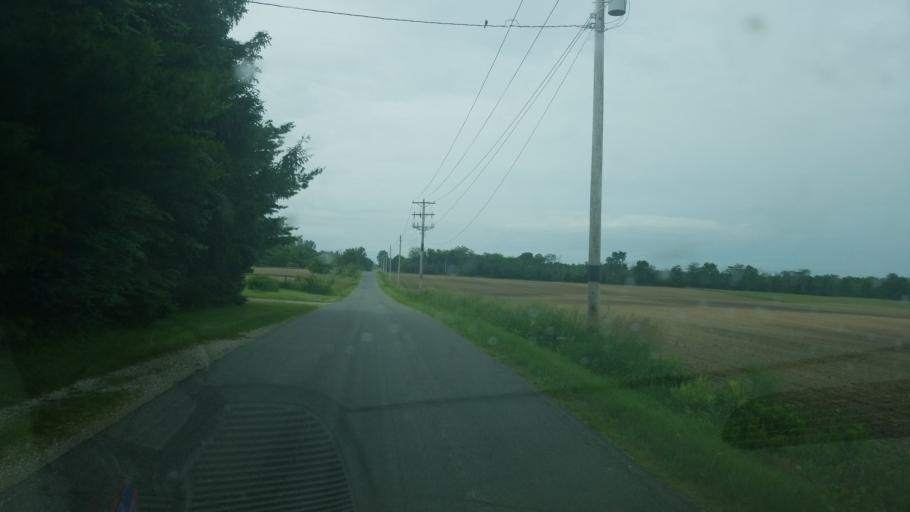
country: US
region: Ohio
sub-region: Crawford County
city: Crestline
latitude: 40.8471
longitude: -82.8181
